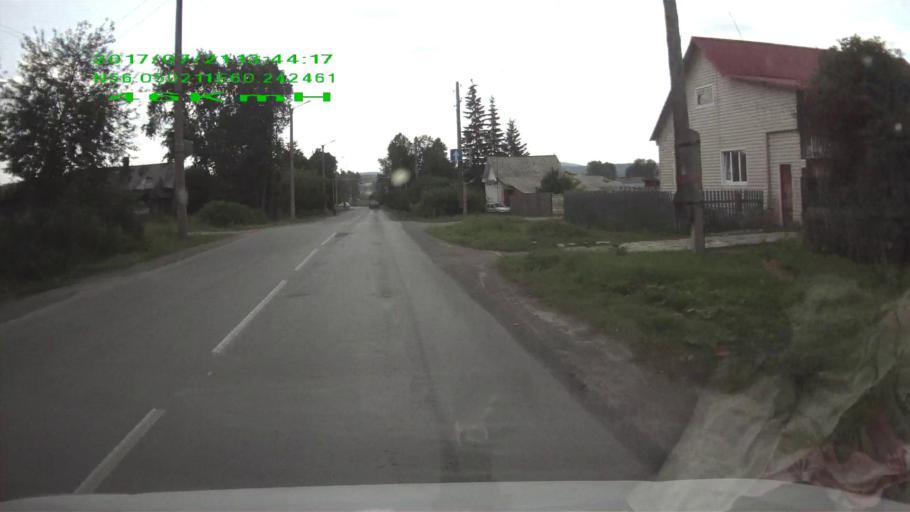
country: RU
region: Chelyabinsk
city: Verkhniy Ufaley
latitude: 56.0497
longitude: 60.2424
